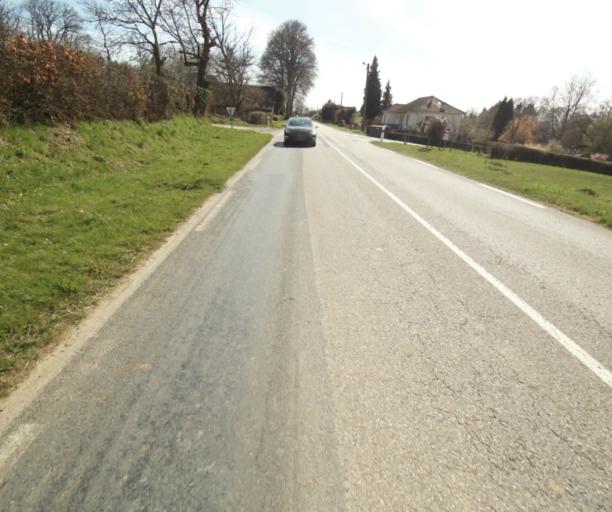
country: FR
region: Limousin
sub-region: Departement de la Correze
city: Seilhac
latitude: 45.3678
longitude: 1.7260
